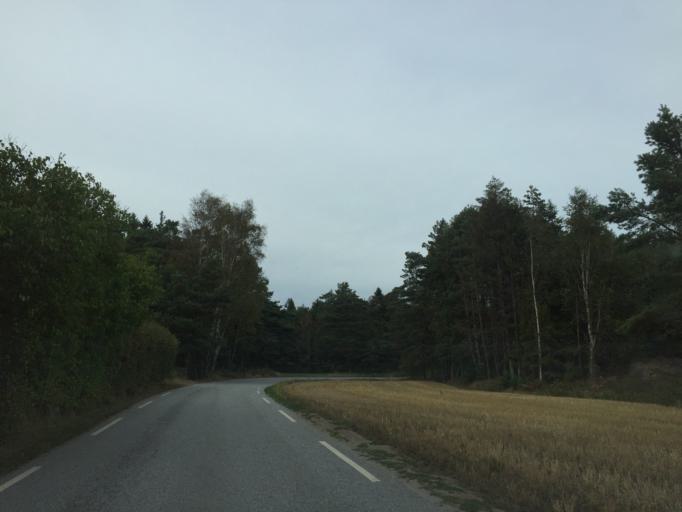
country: NO
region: Ostfold
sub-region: Hvaler
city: Skjaerhalden
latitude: 59.0509
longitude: 11.0466
